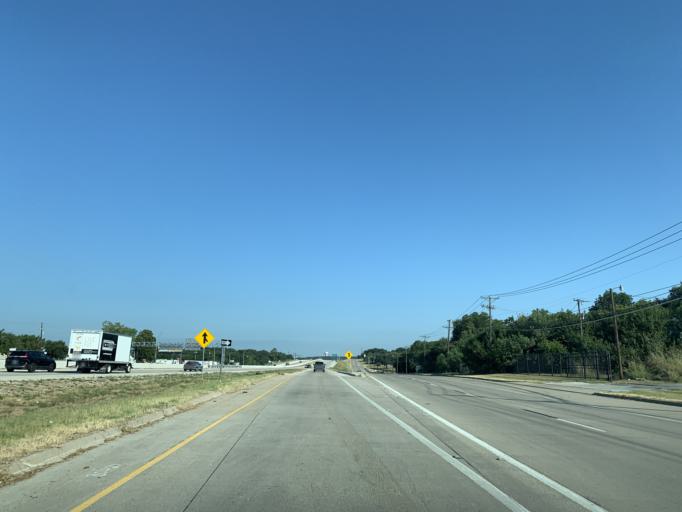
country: US
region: Texas
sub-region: Tarrant County
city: Lakeside
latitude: 32.8411
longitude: -97.4946
